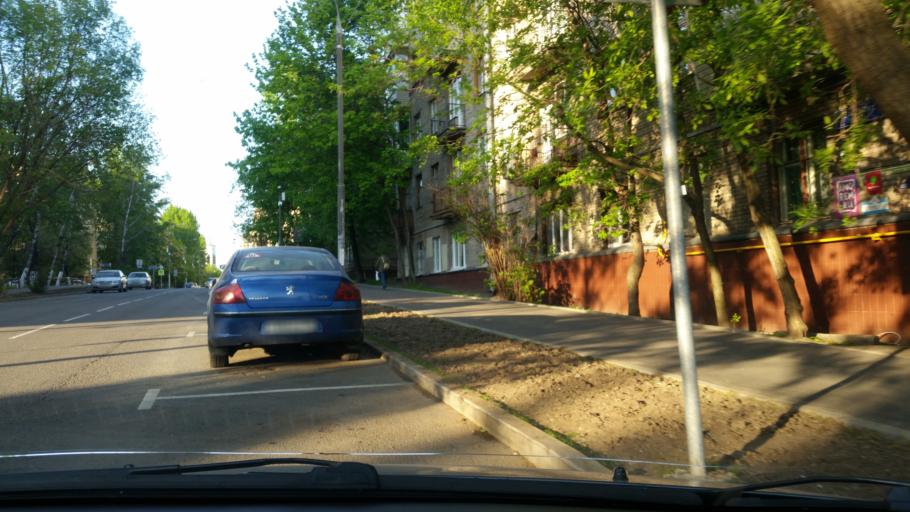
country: RU
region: Moscow
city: Luzhniki
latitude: 55.7211
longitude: 37.5666
